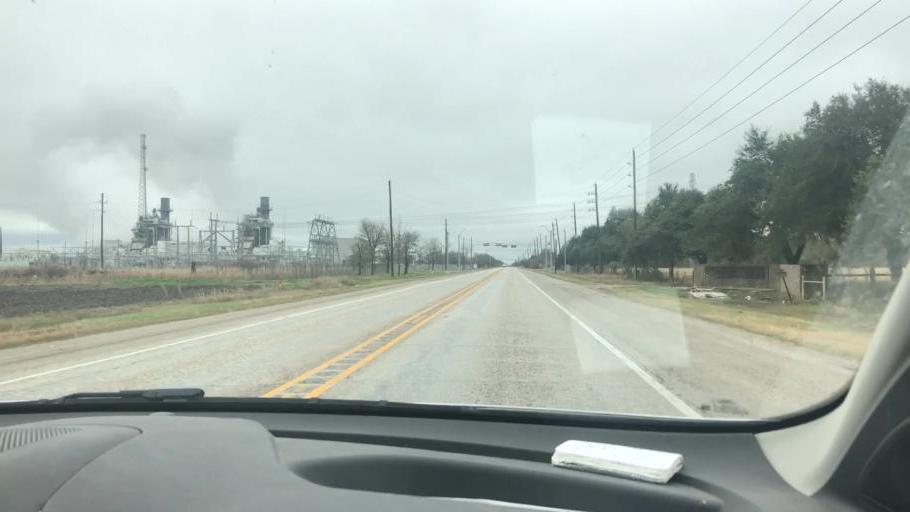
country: US
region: Texas
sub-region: Wharton County
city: Wharton
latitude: 29.2909
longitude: -96.0725
